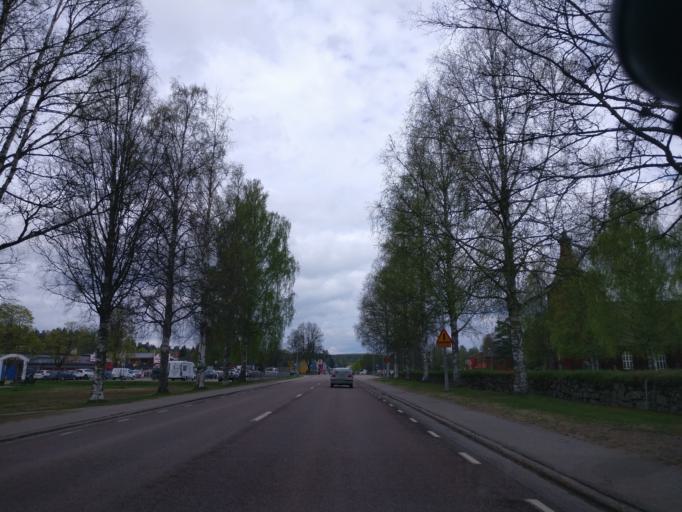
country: SE
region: Vaermland
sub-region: Hagfors Kommun
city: Ekshaerad
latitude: 60.1715
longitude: 13.4968
